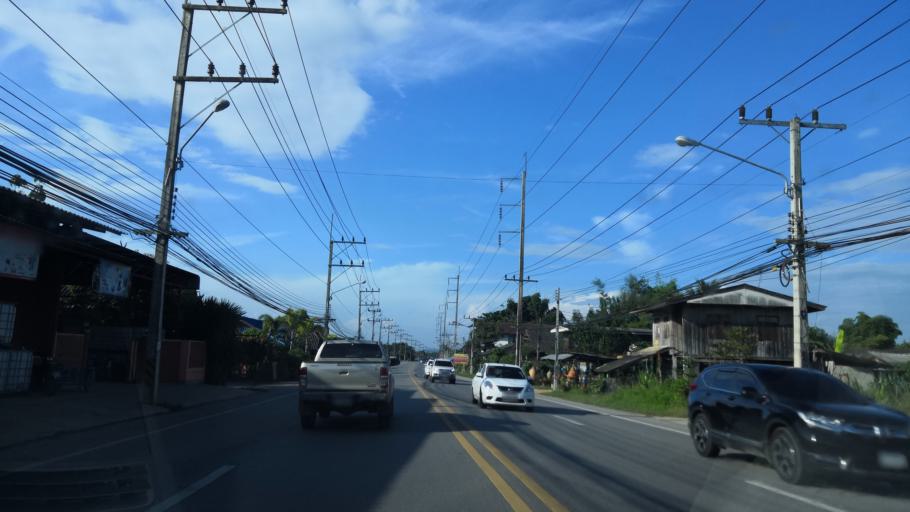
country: TH
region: Chiang Rai
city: Wiang Pa Pao
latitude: 19.3067
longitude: 99.5116
